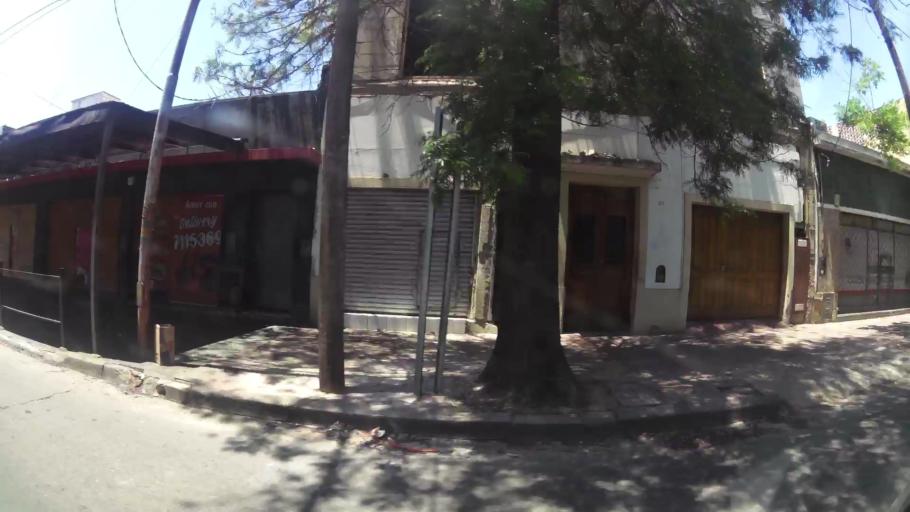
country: AR
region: Cordoba
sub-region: Departamento de Capital
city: Cordoba
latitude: -31.4049
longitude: -64.2178
